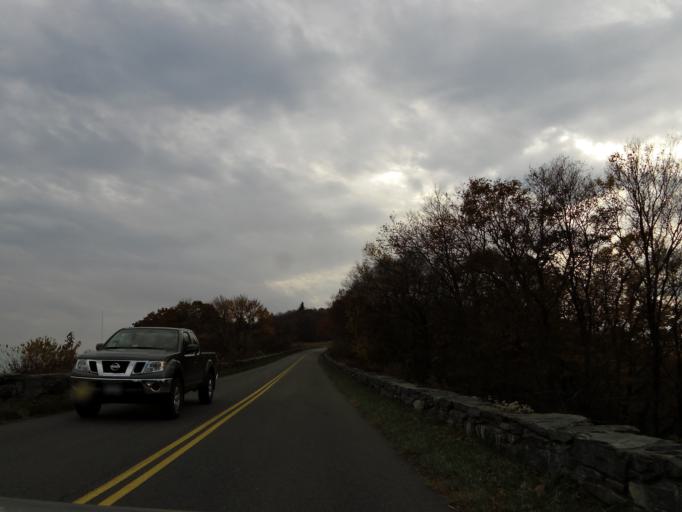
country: US
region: North Carolina
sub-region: Alleghany County
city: Sparta
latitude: 36.4195
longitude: -81.1928
